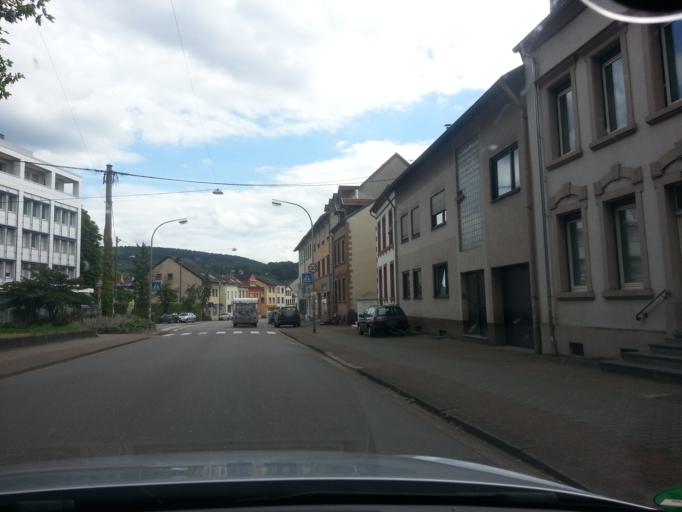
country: DE
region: Saarland
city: Merzig
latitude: 49.4486
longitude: 6.6364
